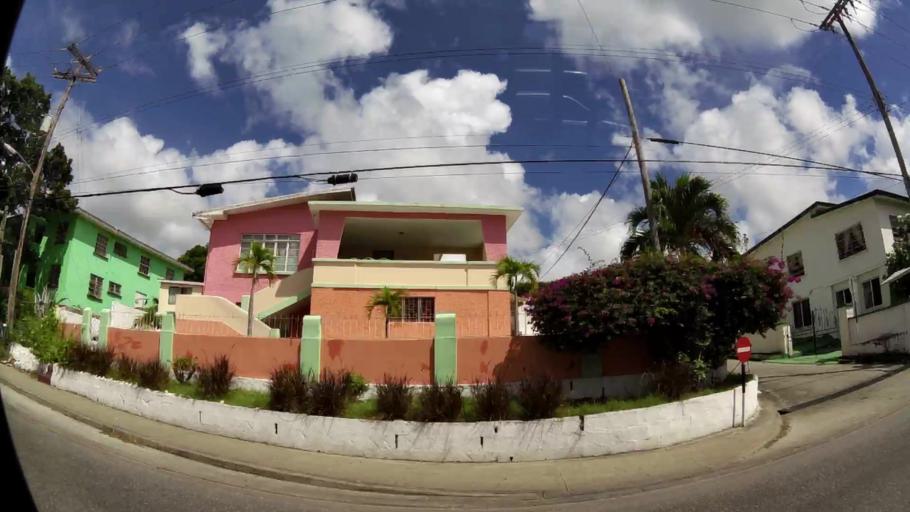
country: BB
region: Saint Michael
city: Bridgetown
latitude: 13.1274
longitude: -59.6279
